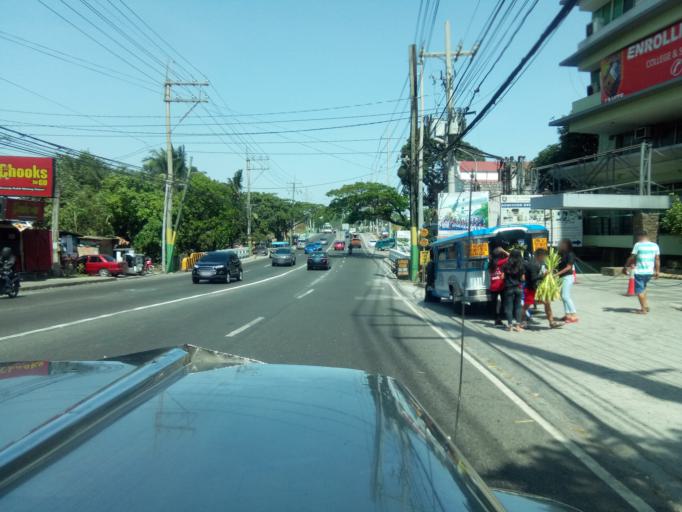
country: PH
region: Calabarzon
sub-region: Province of Cavite
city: Dasmarinas
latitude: 14.2938
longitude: 120.9390
